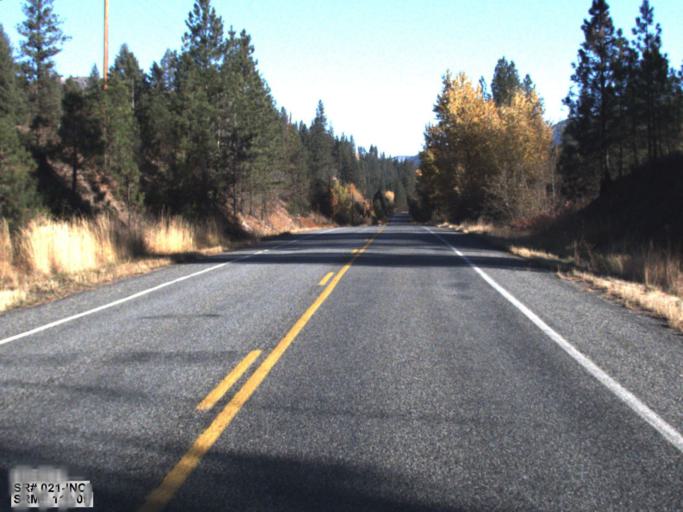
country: US
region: Washington
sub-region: Okanogan County
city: Coulee Dam
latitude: 48.1090
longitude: -118.6994
